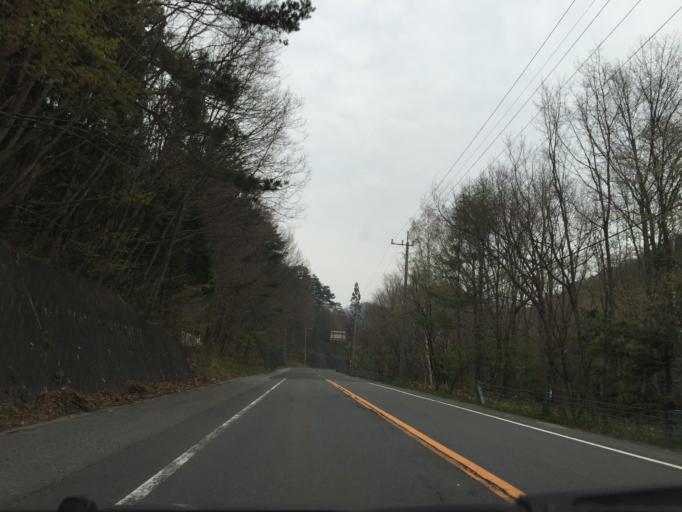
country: JP
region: Tochigi
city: Kuroiso
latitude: 37.0642
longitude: 139.7431
